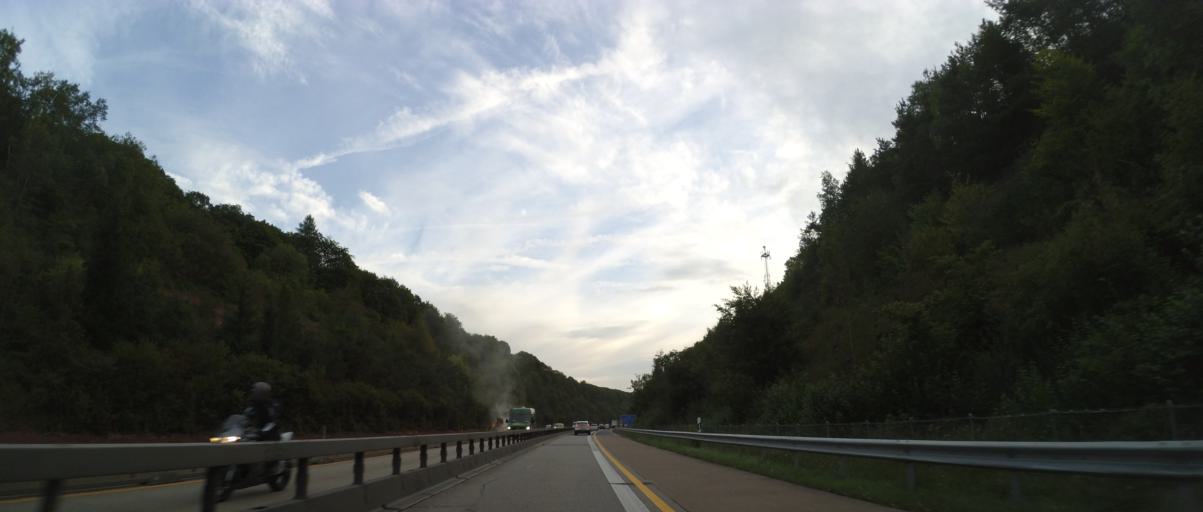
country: DE
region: Rheinland-Pfalz
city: Wittlich
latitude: 49.9591
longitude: 6.8844
